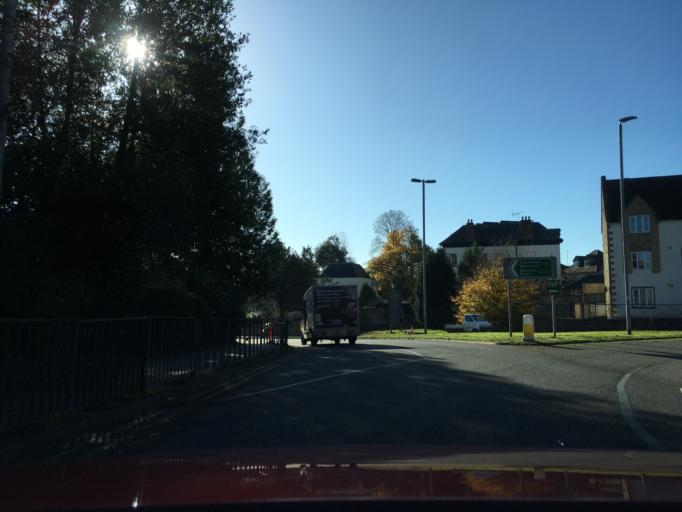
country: GB
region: England
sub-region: Somerset
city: Yeovil
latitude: 50.9461
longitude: -2.6368
